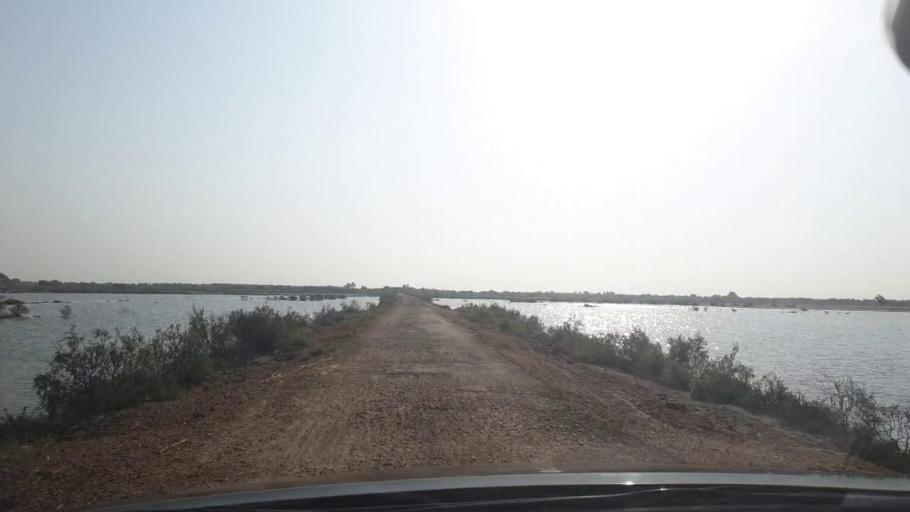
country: PK
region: Sindh
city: Tando Bago
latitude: 24.6510
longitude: 69.1314
